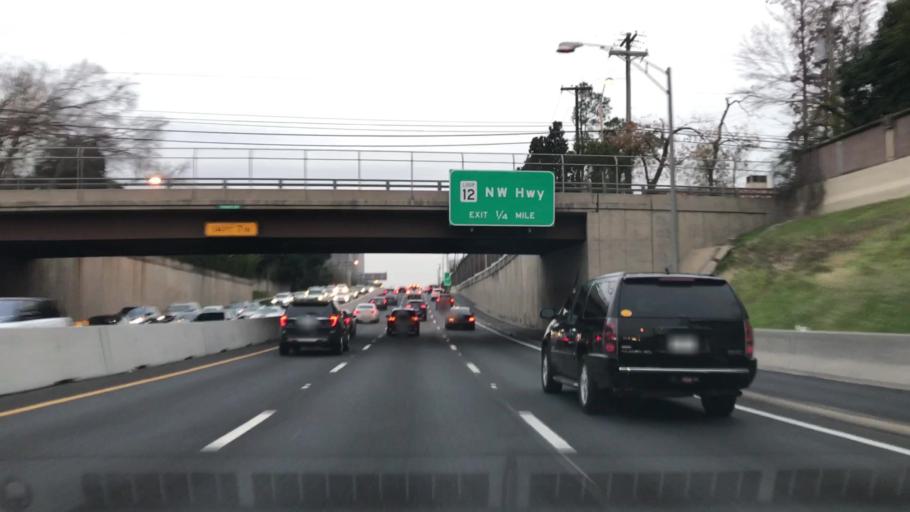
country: US
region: Texas
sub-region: Dallas County
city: University Park
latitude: 32.8743
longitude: -96.8105
